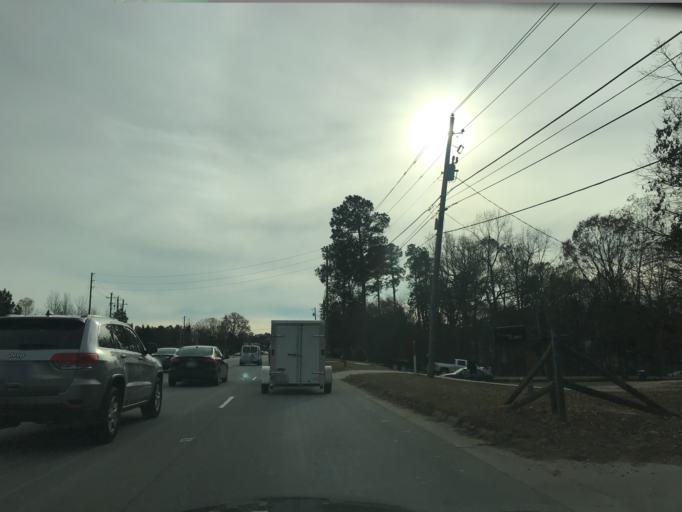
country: US
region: North Carolina
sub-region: Wake County
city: Knightdale
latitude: 35.8668
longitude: -78.5462
